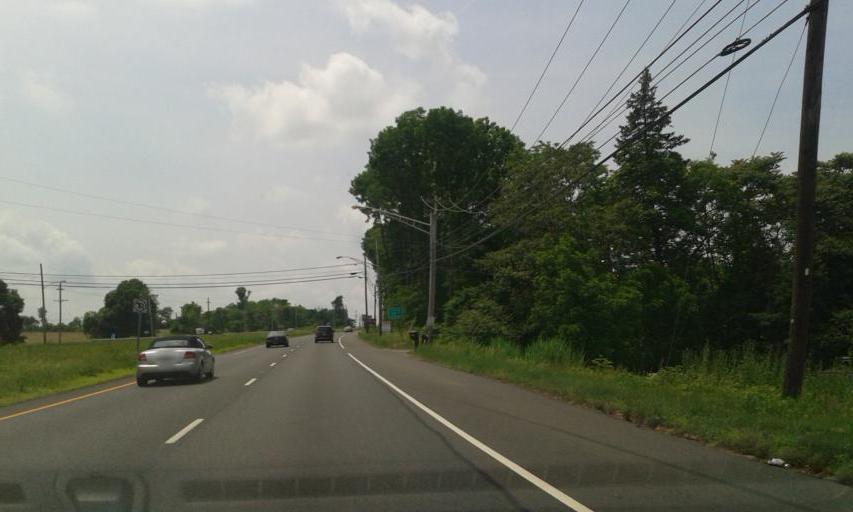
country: US
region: New Jersey
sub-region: Hunterdon County
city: Lebanon
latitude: 40.6436
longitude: -74.8450
